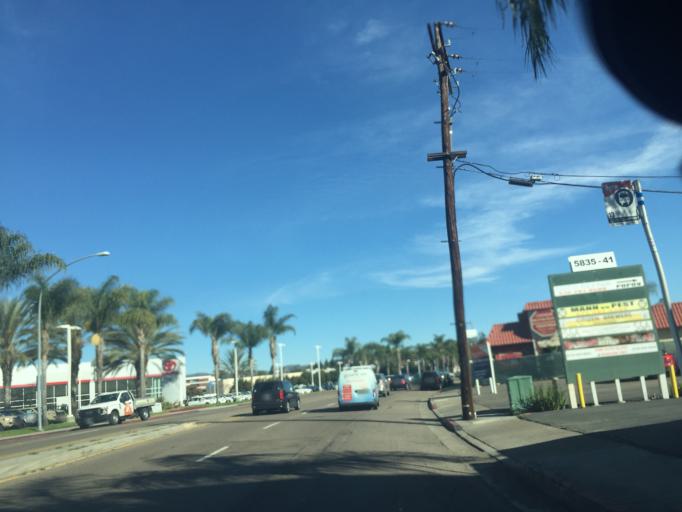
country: US
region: California
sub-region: San Diego County
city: La Mesa
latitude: 32.7816
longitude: -117.1010
